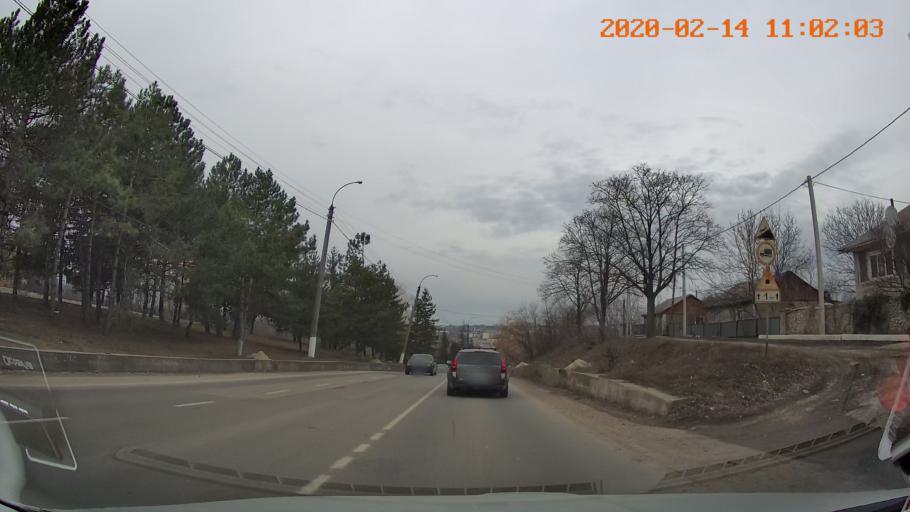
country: MD
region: Raionul Edinet
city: Edinet
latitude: 48.1628
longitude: 27.3235
